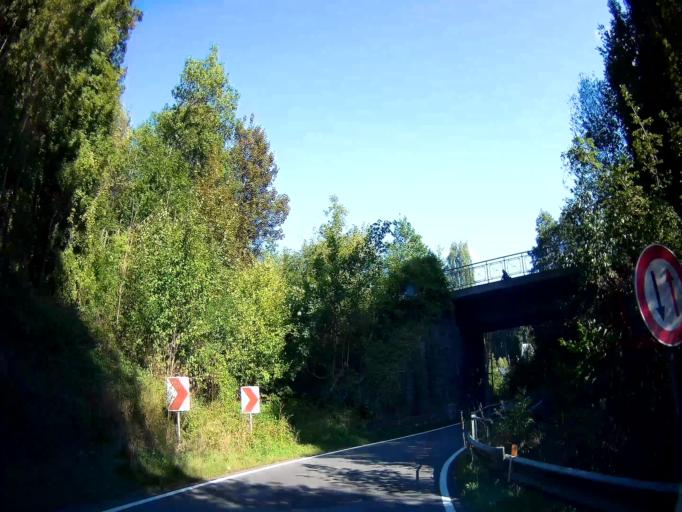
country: BE
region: Wallonia
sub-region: Province de Namur
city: Onhaye
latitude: 50.2922
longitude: 4.8109
